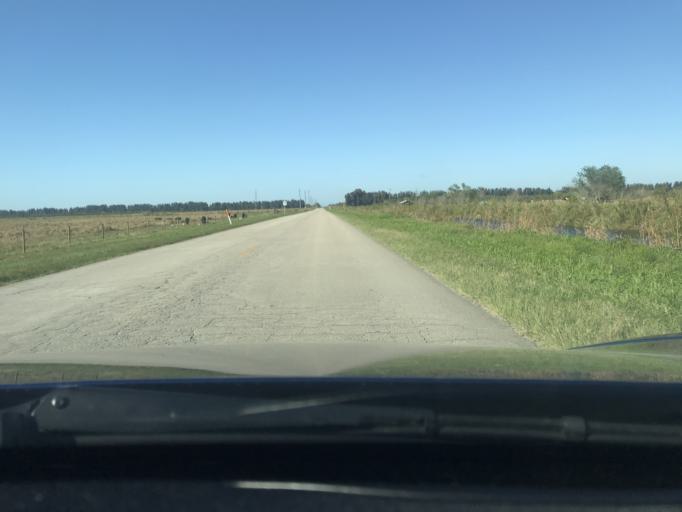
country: US
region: Florida
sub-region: Saint Lucie County
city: Lakewood Park
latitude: 27.4167
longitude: -80.4975
